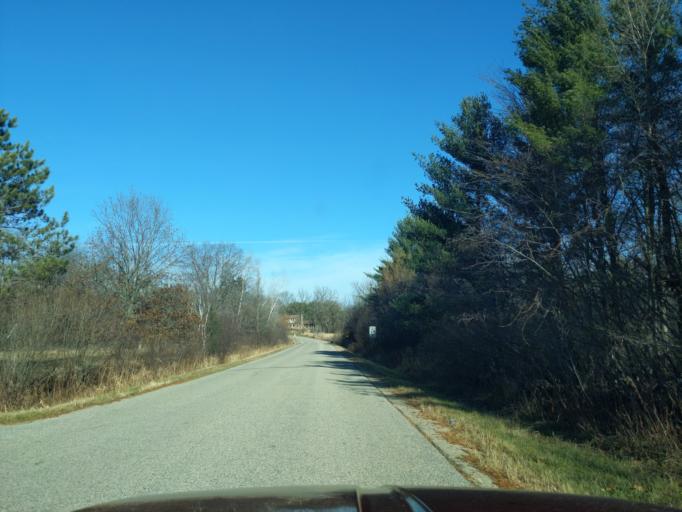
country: US
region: Wisconsin
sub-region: Waushara County
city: Silver Lake
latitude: 44.0611
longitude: -89.1887
